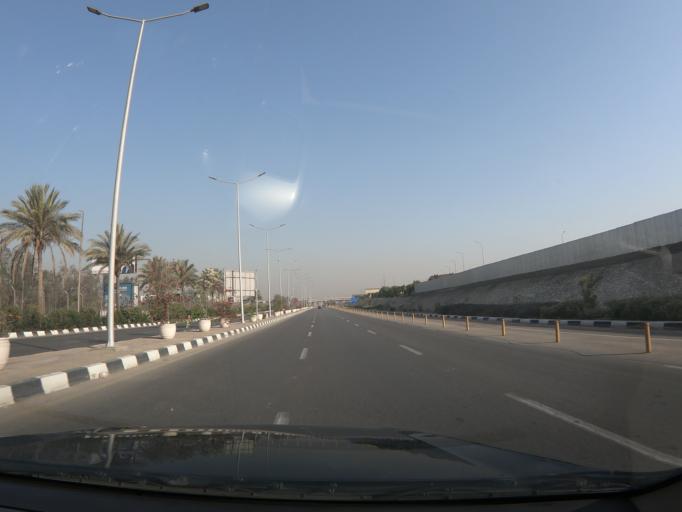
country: EG
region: Muhafazat al Qalyubiyah
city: Al Khankah
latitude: 30.1060
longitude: 31.3869
